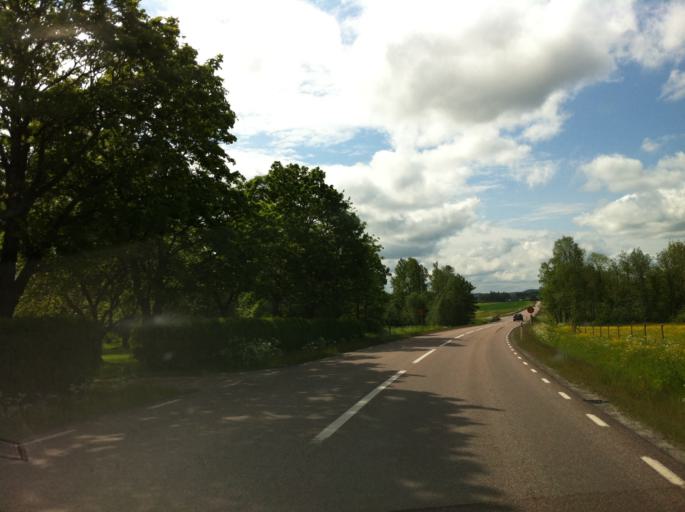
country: SE
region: Vaermland
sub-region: Sunne Kommun
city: Sunne
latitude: 59.6614
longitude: 13.1550
